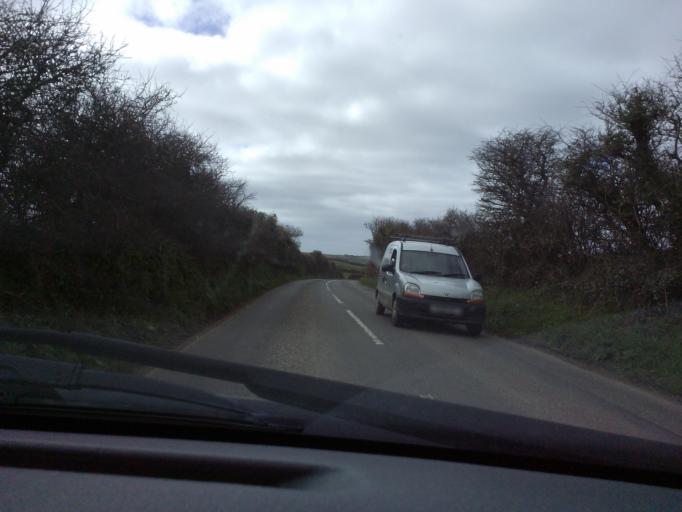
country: GB
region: England
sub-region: Cornwall
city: Penzance
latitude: 50.0792
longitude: -5.5638
